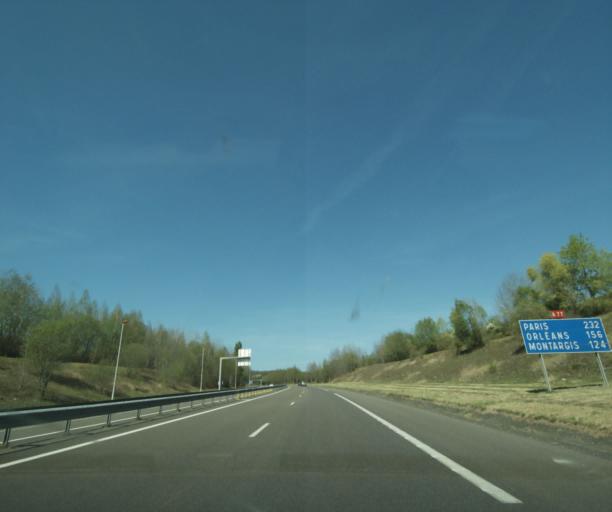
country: FR
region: Bourgogne
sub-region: Departement de la Nievre
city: Coulanges-les-Nevers
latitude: 47.0158
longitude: 3.1992
